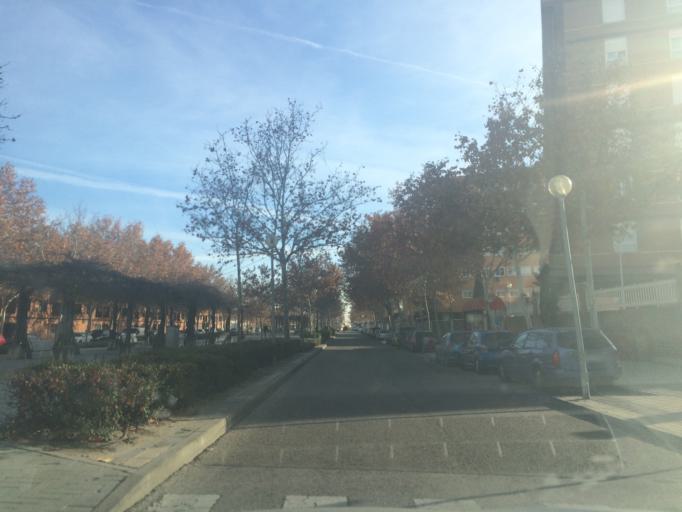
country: ES
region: Madrid
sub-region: Provincia de Madrid
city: Tres Cantos
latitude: 40.5986
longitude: -3.7113
